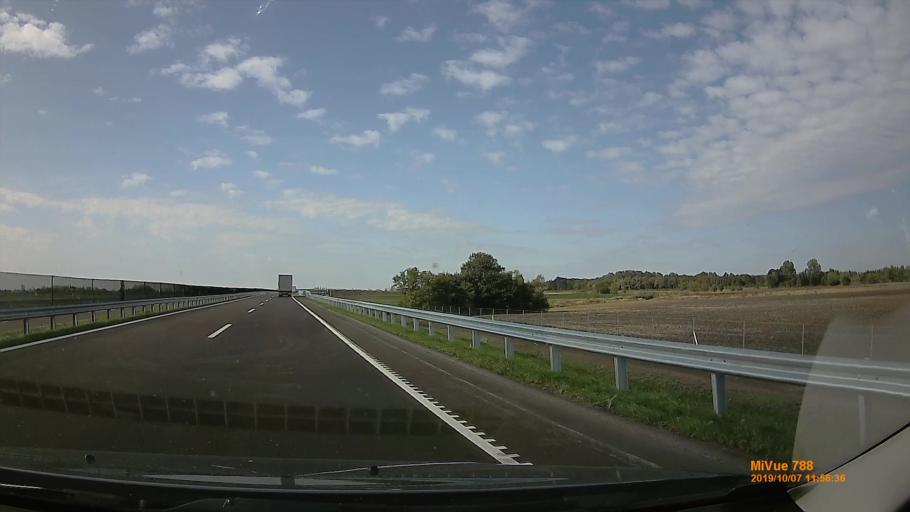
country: HU
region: Bekes
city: Szarvas
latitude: 46.8174
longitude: 20.5498
